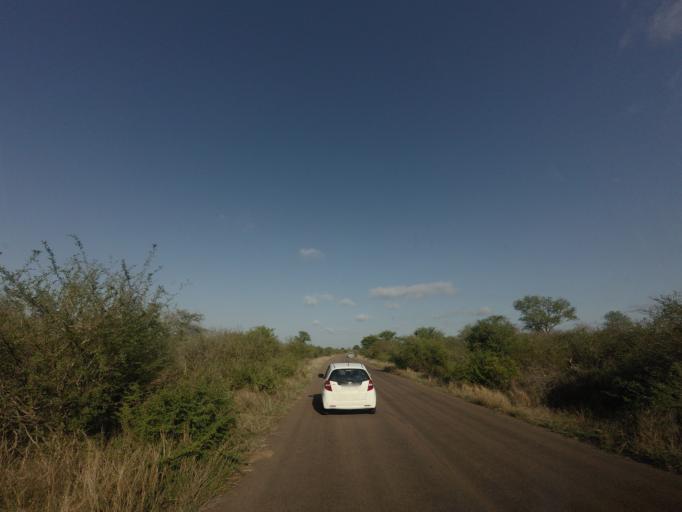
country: ZA
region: Mpumalanga
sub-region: Ehlanzeni District
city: Komatipoort
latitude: -25.2847
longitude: 31.8579
